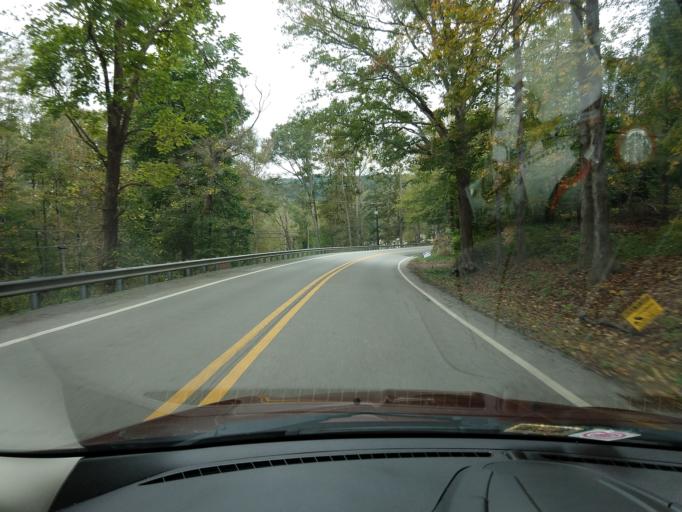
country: US
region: West Virginia
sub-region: Barbour County
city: Belington
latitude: 39.0214
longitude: -79.9374
